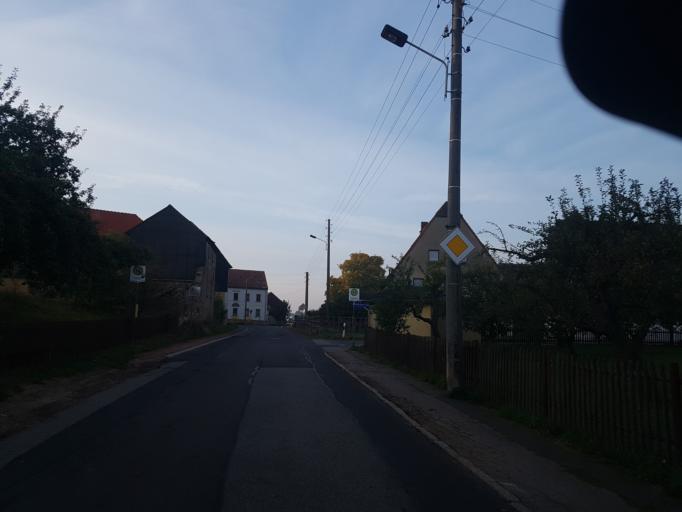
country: DE
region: Saxony
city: Waldheim
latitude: 51.1024
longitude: 13.0570
